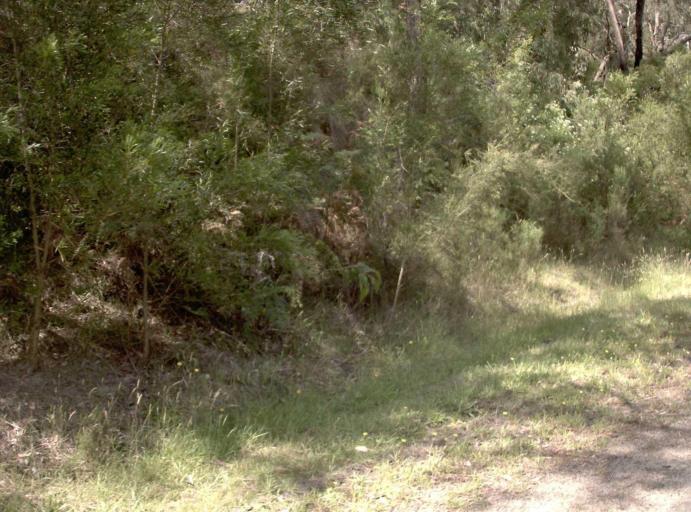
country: AU
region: Victoria
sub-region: Latrobe
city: Traralgon
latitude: -38.3067
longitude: 146.5479
